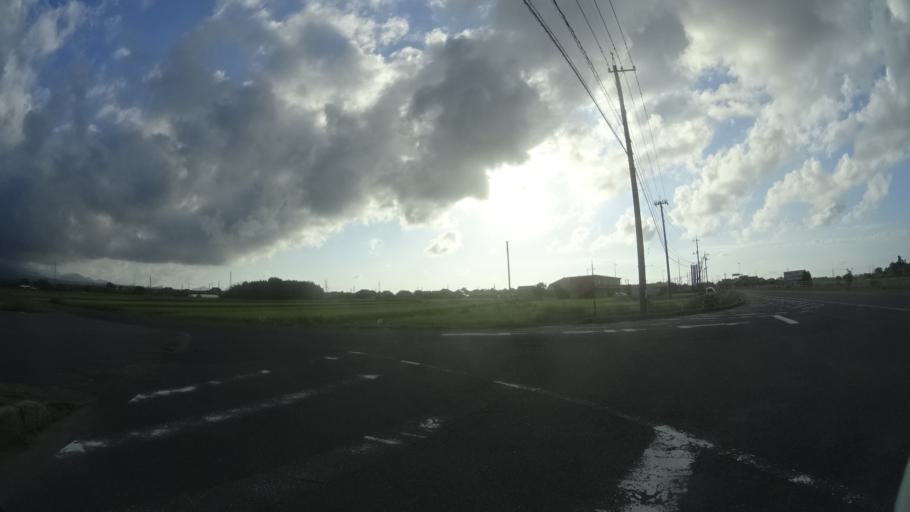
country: JP
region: Tottori
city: Kurayoshi
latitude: 35.5228
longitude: 133.5953
